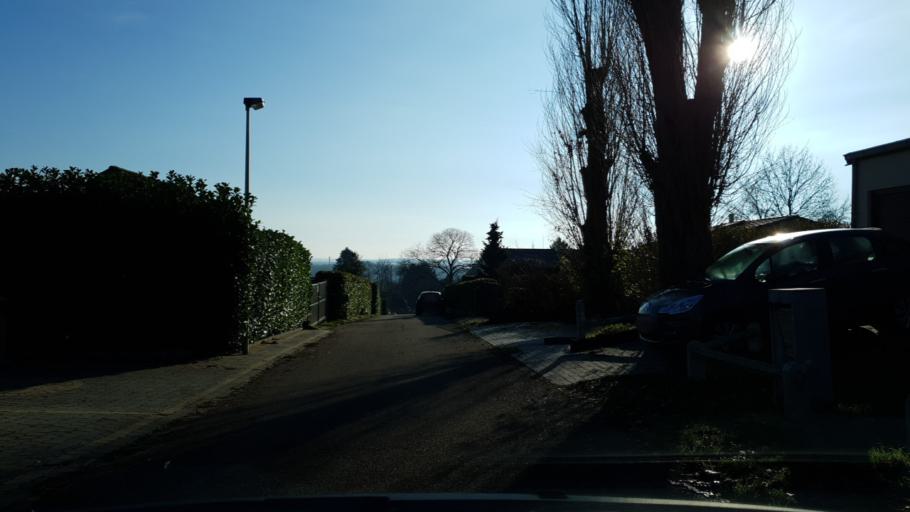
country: BE
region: Flanders
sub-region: Provincie Vlaams-Brabant
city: Bertem
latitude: 50.8718
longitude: 4.6036
